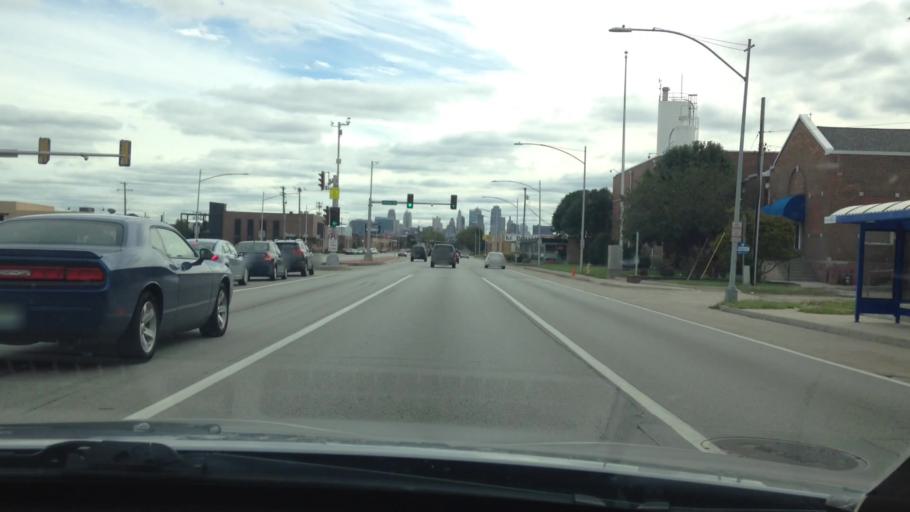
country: US
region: Missouri
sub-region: Clay County
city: North Kansas City
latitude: 39.1420
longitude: -94.5805
